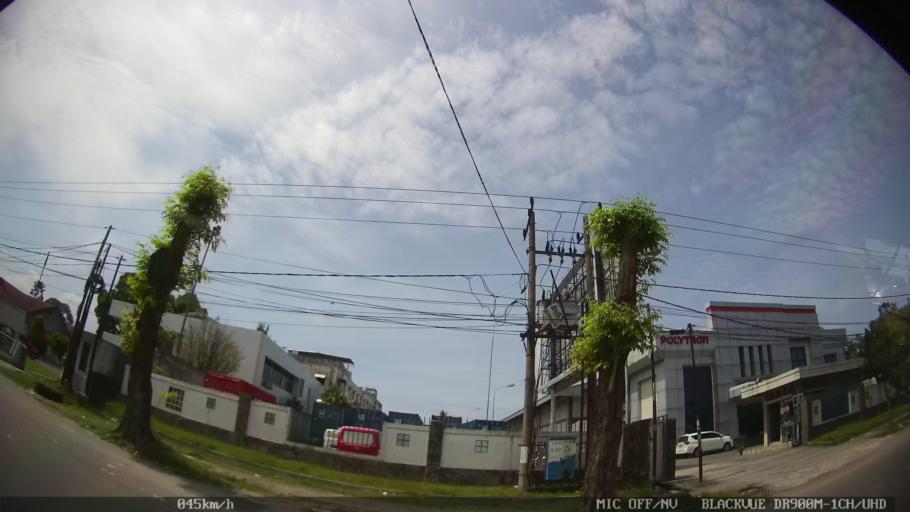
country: ID
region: North Sumatra
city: Sunggal
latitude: 3.5913
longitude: 98.6312
